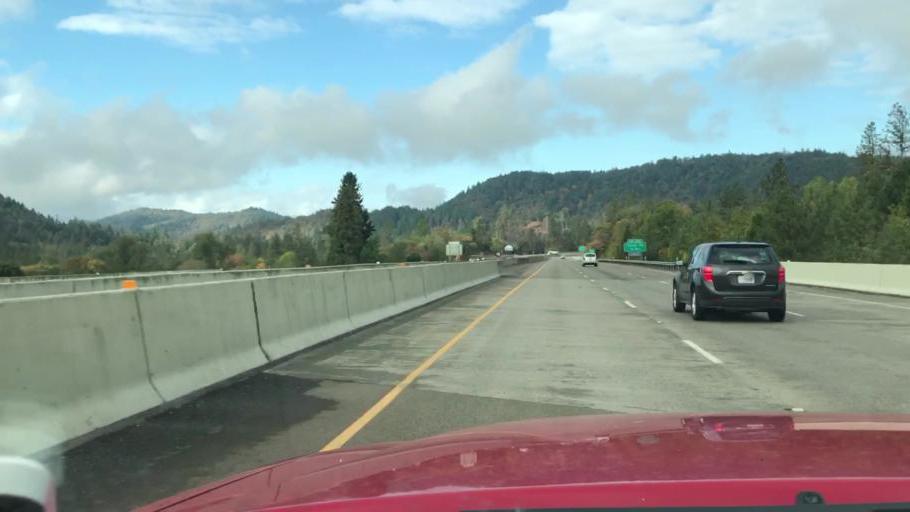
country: US
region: Oregon
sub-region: Douglas County
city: Tri-City
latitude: 42.9480
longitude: -123.3192
